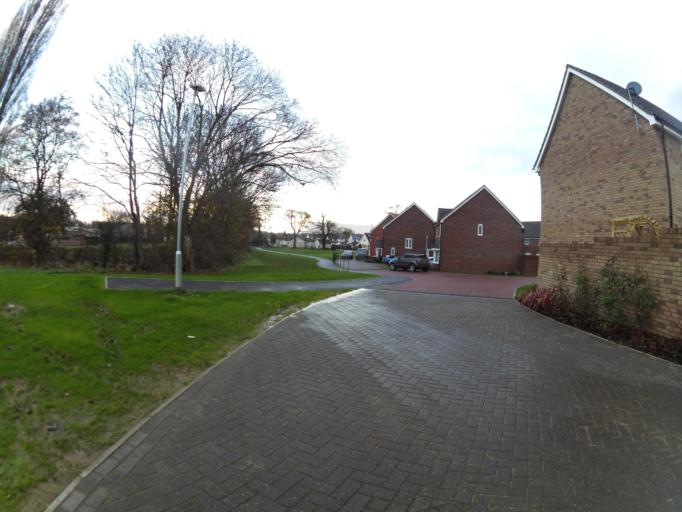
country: GB
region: England
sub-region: Suffolk
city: Bramford
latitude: 52.0593
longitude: 1.0995
